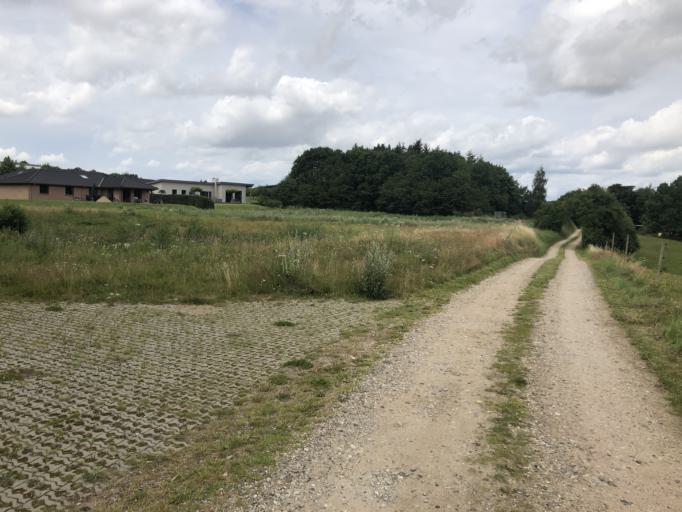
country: DK
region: South Denmark
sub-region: Kolding Kommune
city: Kolding
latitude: 55.5636
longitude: 9.4179
